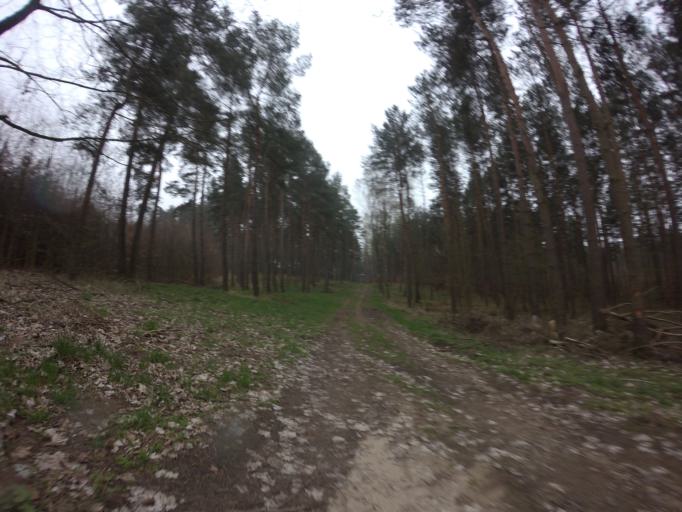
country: PL
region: West Pomeranian Voivodeship
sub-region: Powiat choszczenski
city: Recz
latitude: 53.1905
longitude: 15.5219
